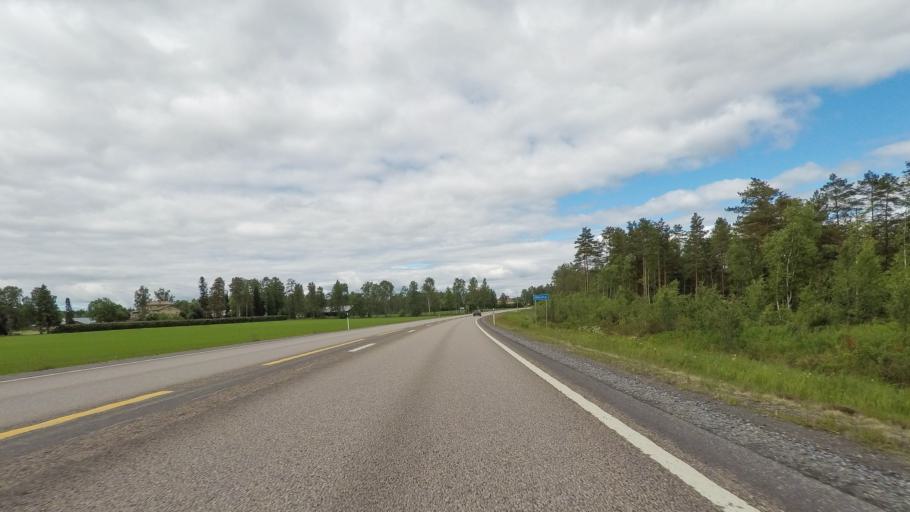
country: FI
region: Paijanne Tavastia
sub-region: Lahti
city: Hartola
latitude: 61.4988
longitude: 25.9798
